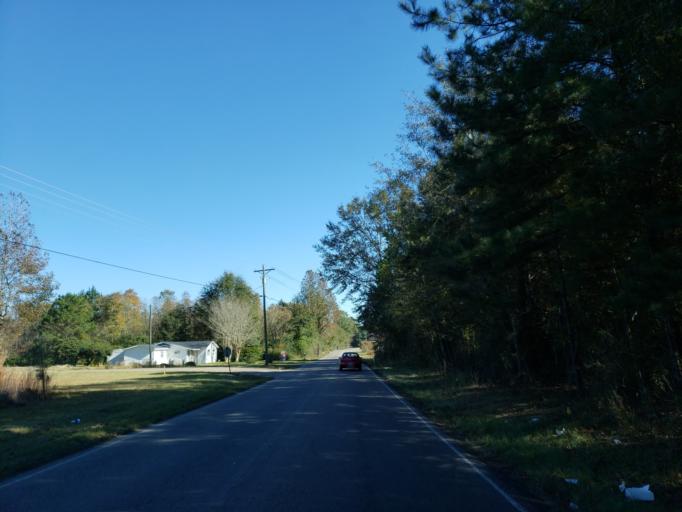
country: US
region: Mississippi
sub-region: Lamar County
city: West Hattiesburg
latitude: 31.3078
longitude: -89.3912
